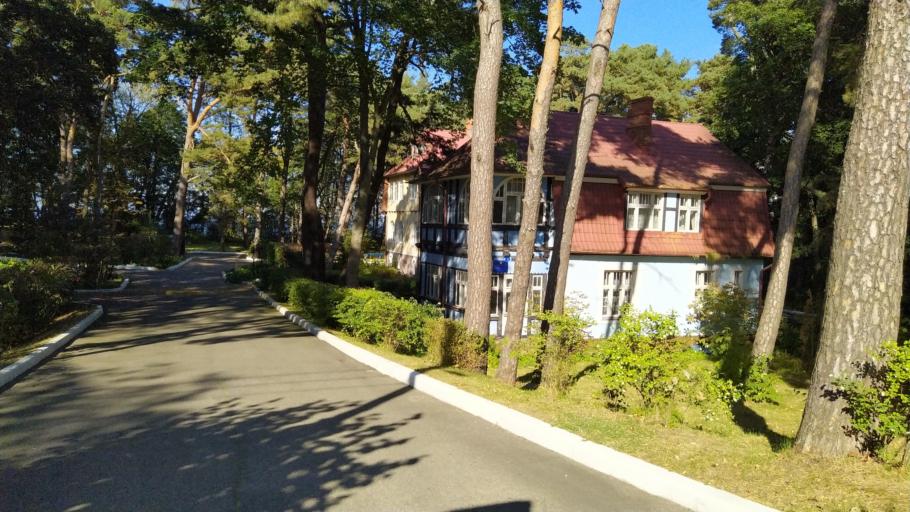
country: RU
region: Kaliningrad
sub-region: Gorod Svetlogorsk
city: Svetlogorsk
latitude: 54.9441
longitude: 20.1457
